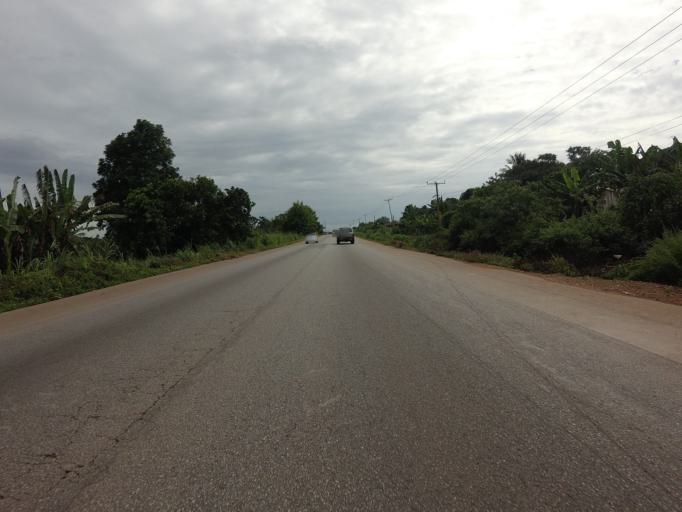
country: GH
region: Eastern
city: Nkawkaw
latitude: 6.6004
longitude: -0.8828
